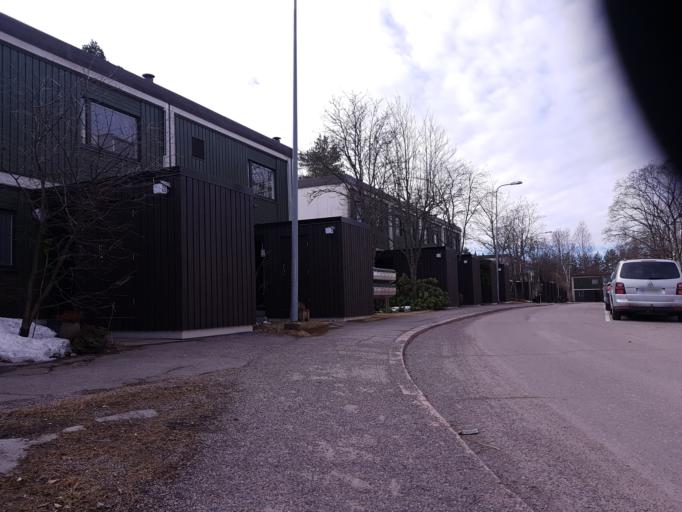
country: FI
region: Uusimaa
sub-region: Helsinki
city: Teekkarikylae
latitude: 60.2370
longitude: 24.8873
